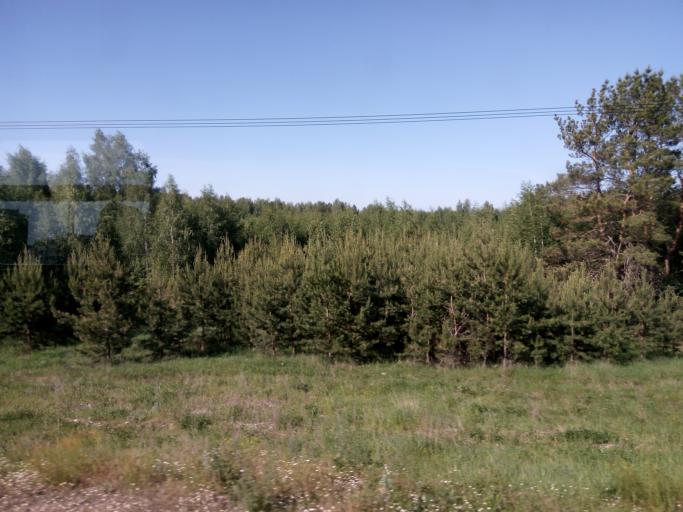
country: RU
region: Tatarstan
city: Stolbishchi
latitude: 55.6905
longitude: 49.1961
